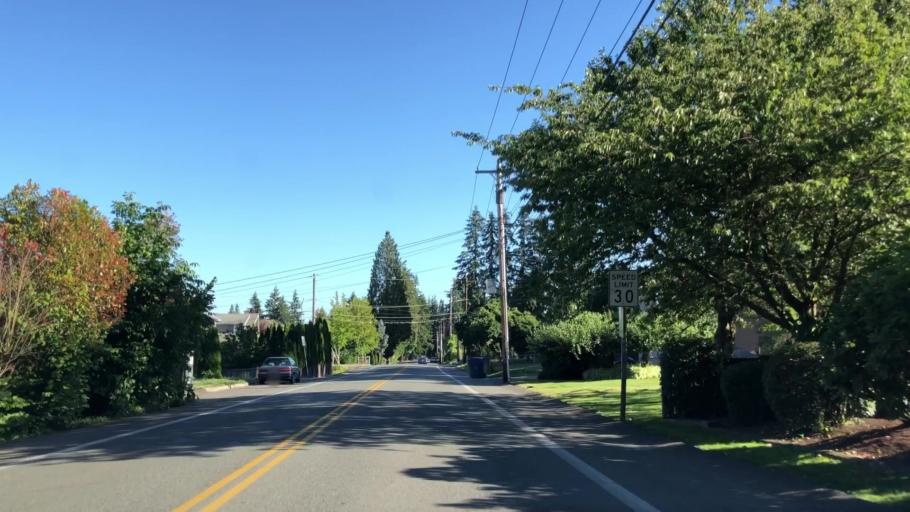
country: US
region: Washington
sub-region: Snohomish County
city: Martha Lake
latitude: 47.8363
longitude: -122.2463
